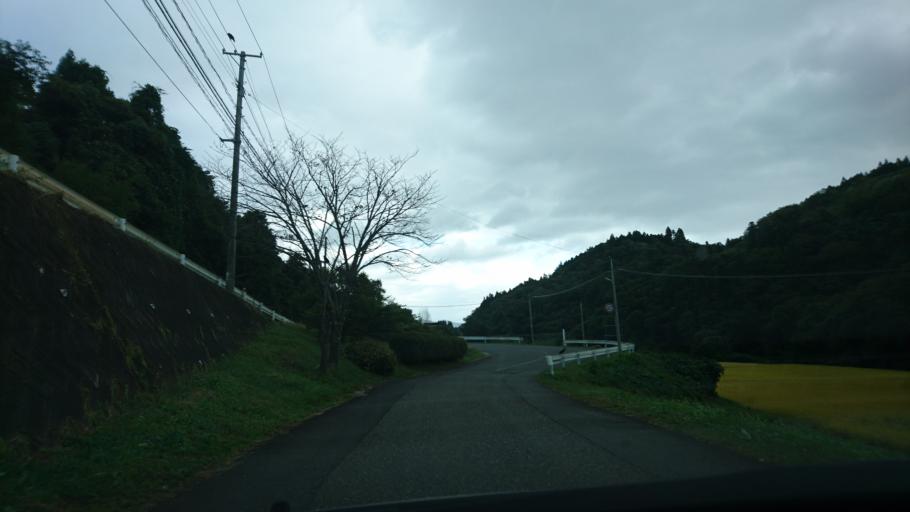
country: JP
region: Iwate
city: Ichinoseki
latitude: 38.9145
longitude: 141.0803
